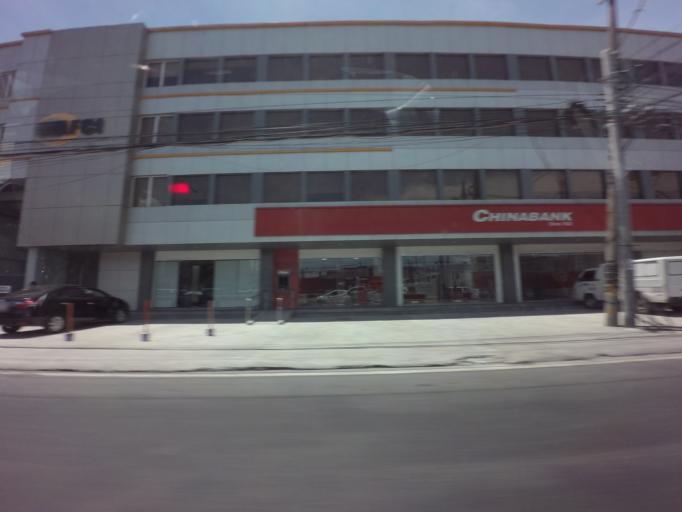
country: PH
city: Sambayanihan People's Village
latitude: 14.4911
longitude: 120.9920
